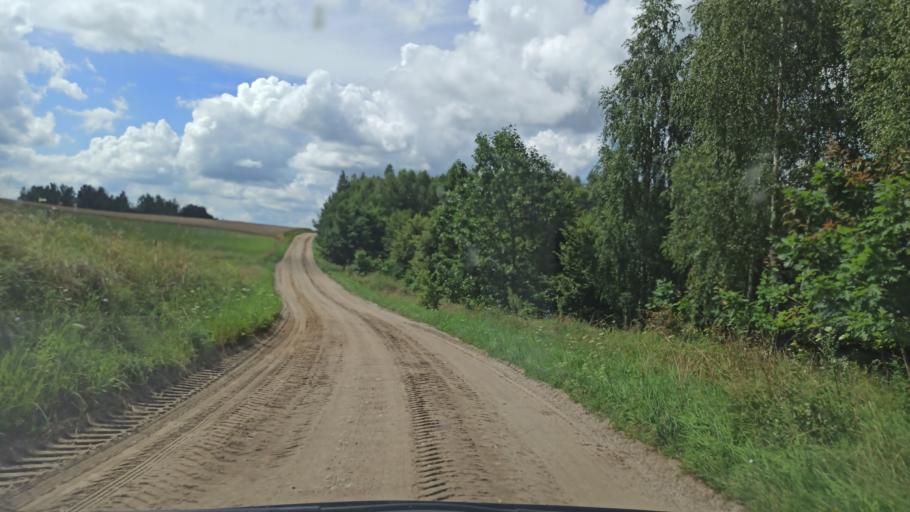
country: PL
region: Warmian-Masurian Voivodeship
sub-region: Powiat ostrodzki
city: Morag
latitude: 53.8634
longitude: 20.0326
